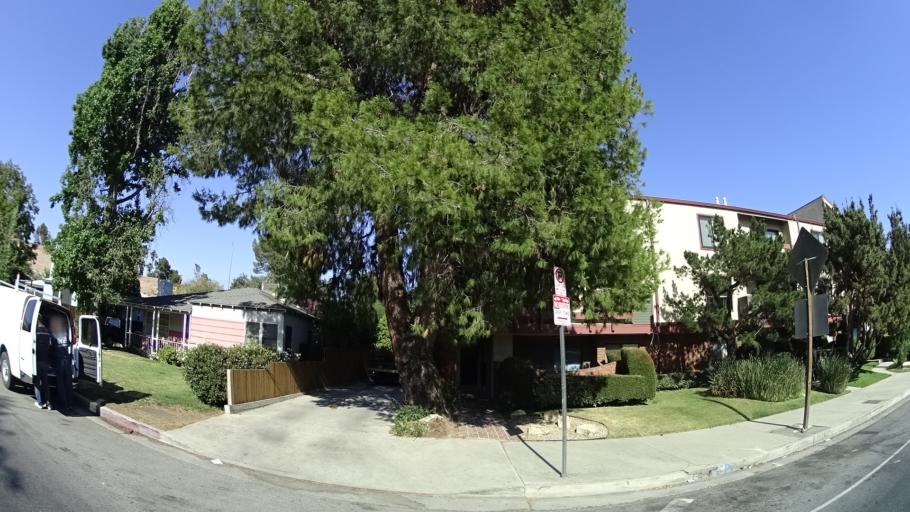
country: US
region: California
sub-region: Los Angeles County
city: North Hollywood
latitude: 34.1529
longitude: -118.3789
